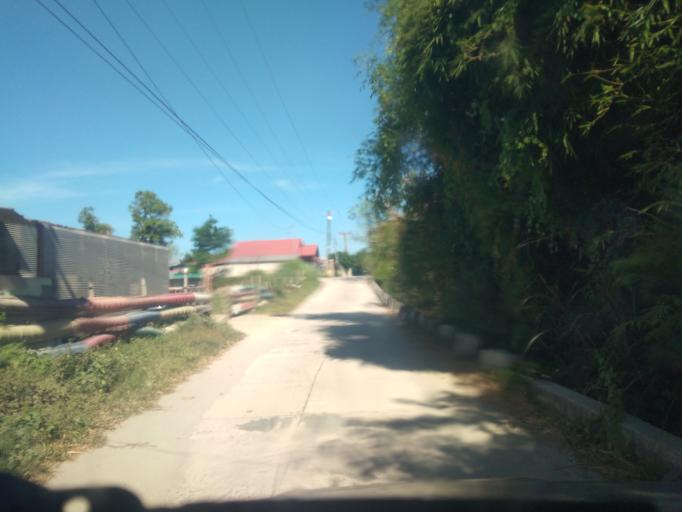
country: PH
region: Central Luzon
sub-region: Province of Pampanga
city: Calibutbut
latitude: 15.0937
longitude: 120.5927
